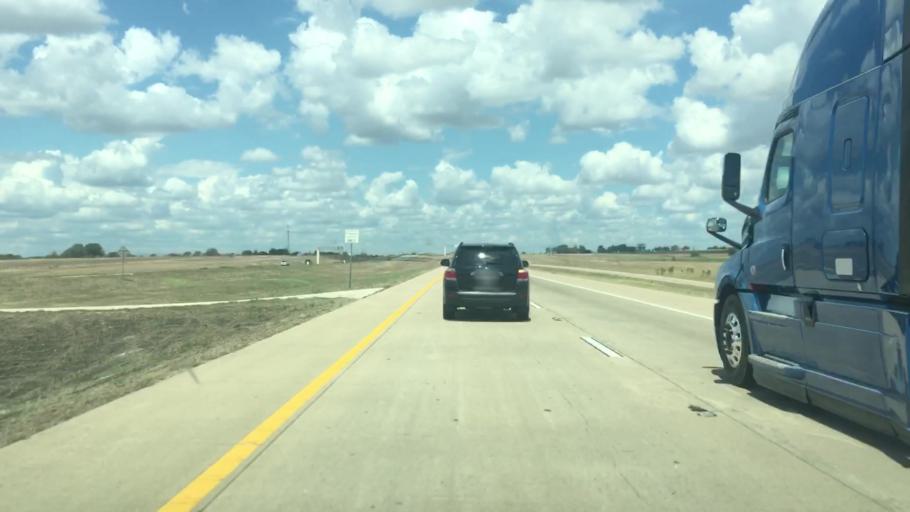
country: US
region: Texas
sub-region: Williamson County
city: Hutto
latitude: 30.5646
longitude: -97.5799
